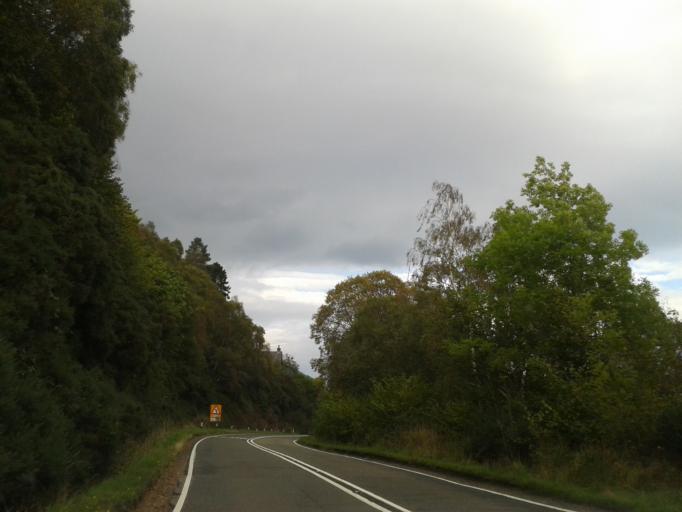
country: GB
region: Scotland
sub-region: Highland
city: Beauly
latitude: 57.3211
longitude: -4.4469
